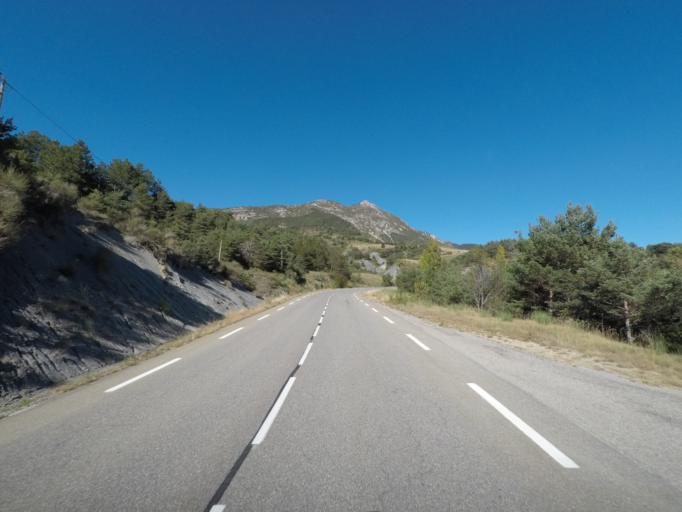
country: FR
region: Provence-Alpes-Cote d'Azur
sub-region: Departement des Hautes-Alpes
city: Serres
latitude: 44.4054
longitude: 5.5278
